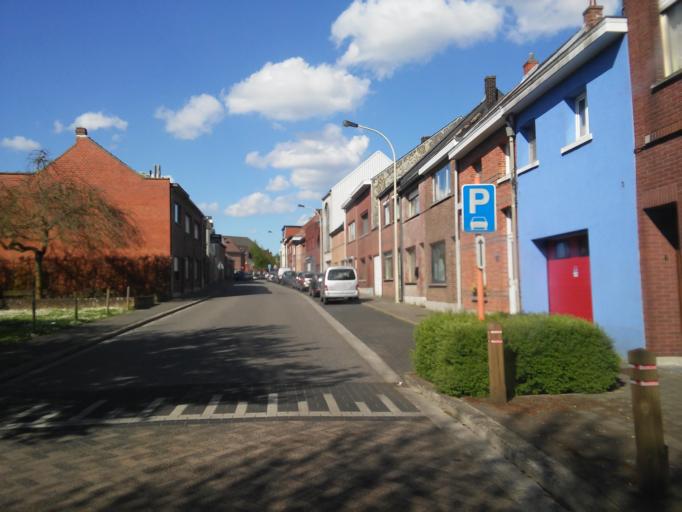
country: BE
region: Flanders
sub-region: Provincie Antwerpen
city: Boom
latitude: 51.0878
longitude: 4.3892
